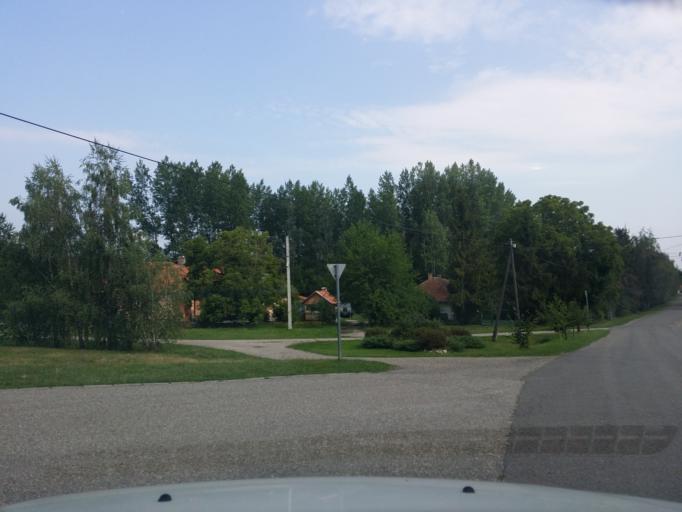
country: HU
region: Borsod-Abauj-Zemplen
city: Satoraljaujhely
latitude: 48.4615
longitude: 21.5902
